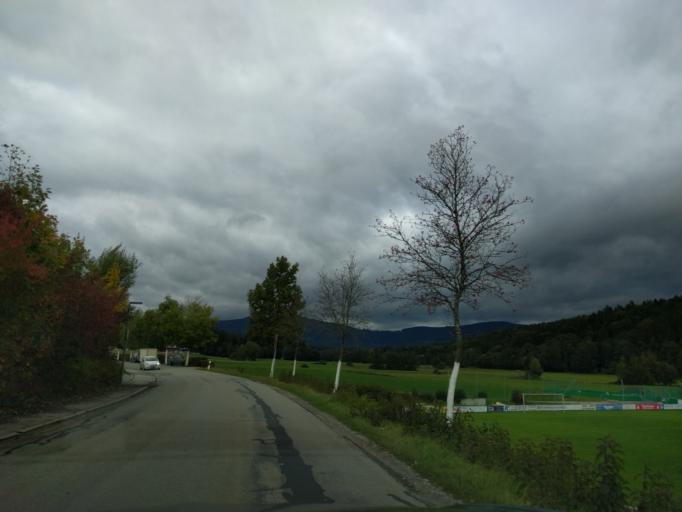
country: DE
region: Bavaria
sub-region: Lower Bavaria
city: Auerbach
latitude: 48.8062
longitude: 13.0945
